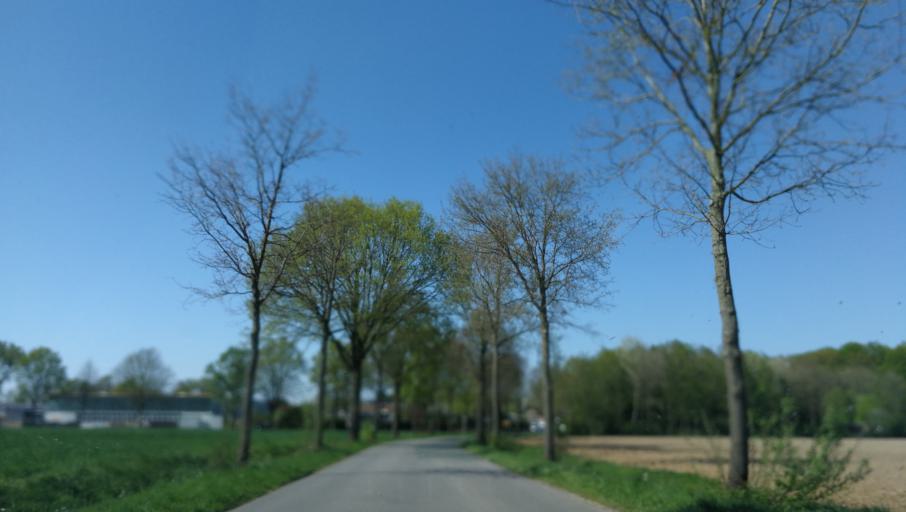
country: DE
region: North Rhine-Westphalia
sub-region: Regierungsbezirk Munster
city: Muenster
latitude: 51.9425
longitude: 7.5385
